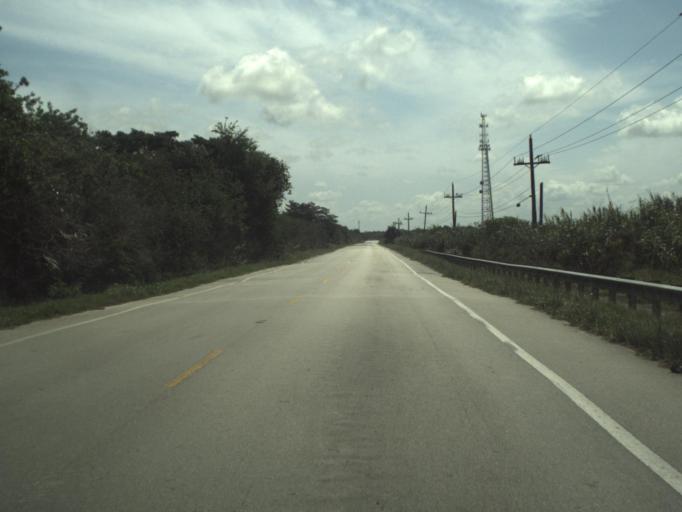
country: US
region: Florida
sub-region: Martin County
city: Indiantown
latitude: 26.9854
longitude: -80.6123
